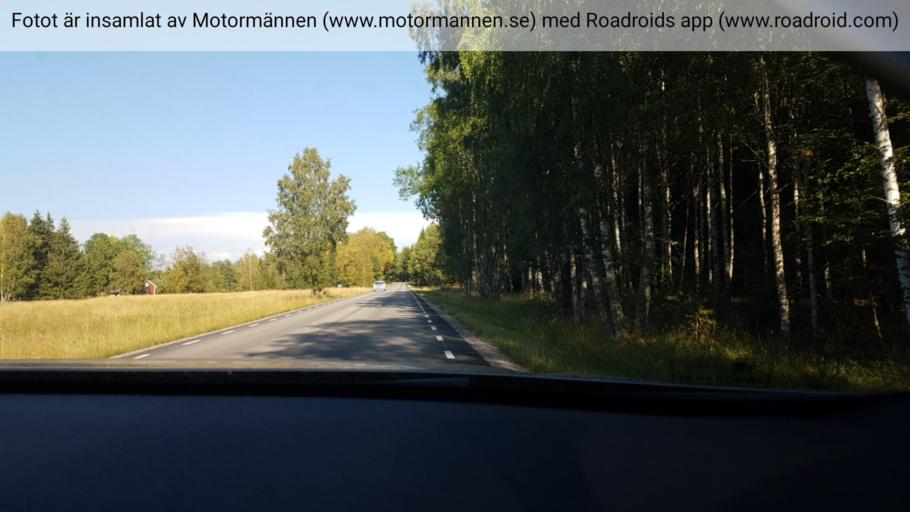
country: SE
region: Vaestra Goetaland
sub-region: Gotene Kommun
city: Goetene
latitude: 58.6309
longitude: 13.5145
